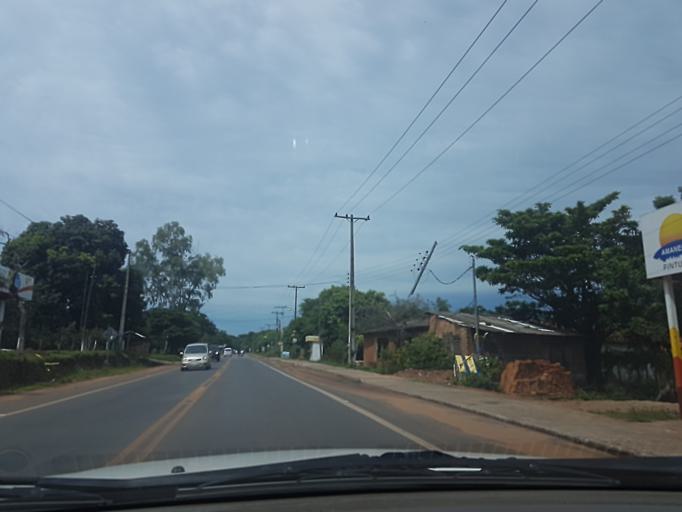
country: PY
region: Central
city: Limpio
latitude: -25.2528
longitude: -57.4617
